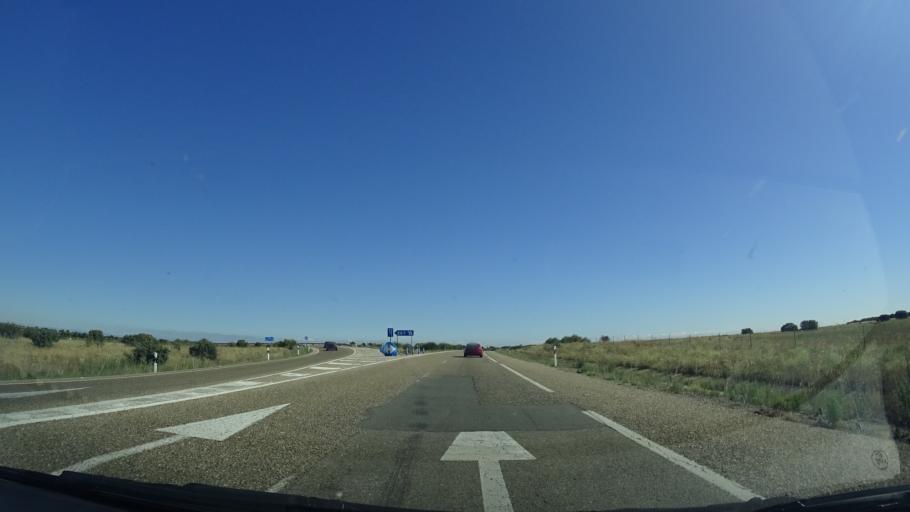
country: ES
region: Castille and Leon
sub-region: Provincia de Zamora
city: San Cristobal de Entrevinas
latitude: 42.0552
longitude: -5.6754
